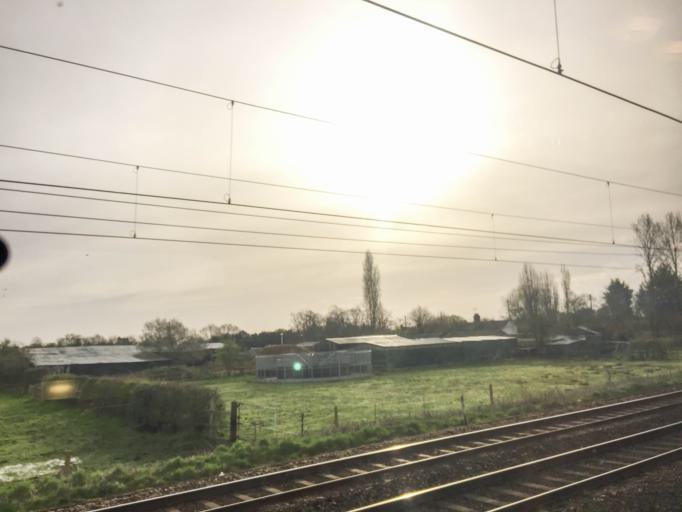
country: GB
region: England
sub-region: Cheshire East
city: Crewe
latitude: 53.1198
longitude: -2.4502
